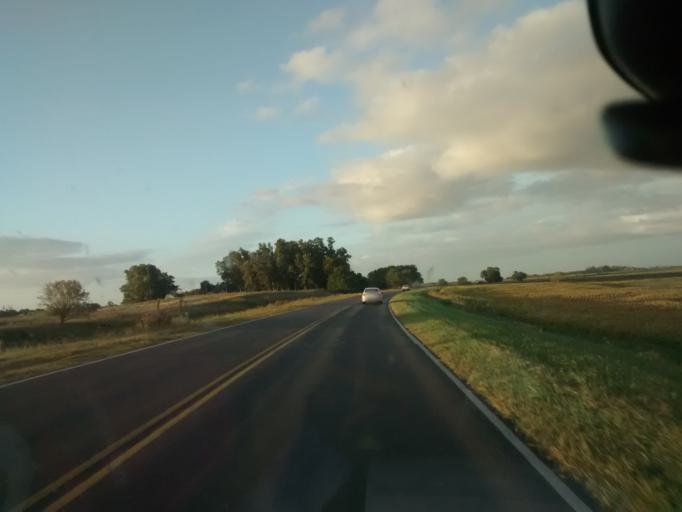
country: AR
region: Buenos Aires
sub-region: Partido de General Belgrano
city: General Belgrano
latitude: -35.6757
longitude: -58.4783
